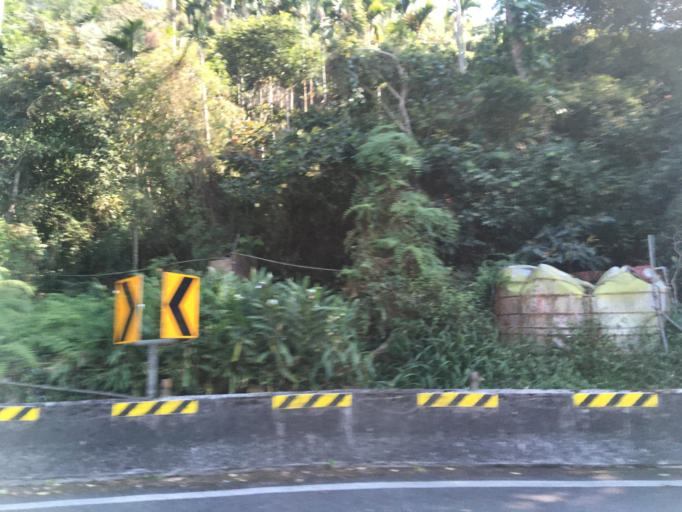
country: TW
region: Taiwan
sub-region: Chiayi
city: Jiayi Shi
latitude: 23.4252
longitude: 120.6429
